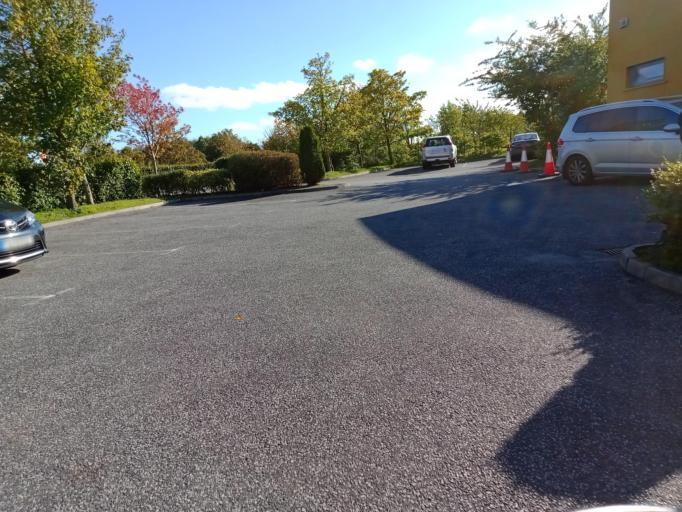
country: IE
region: Leinster
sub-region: Kilkenny
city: Kilkenny
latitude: 52.6351
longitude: -7.2385
